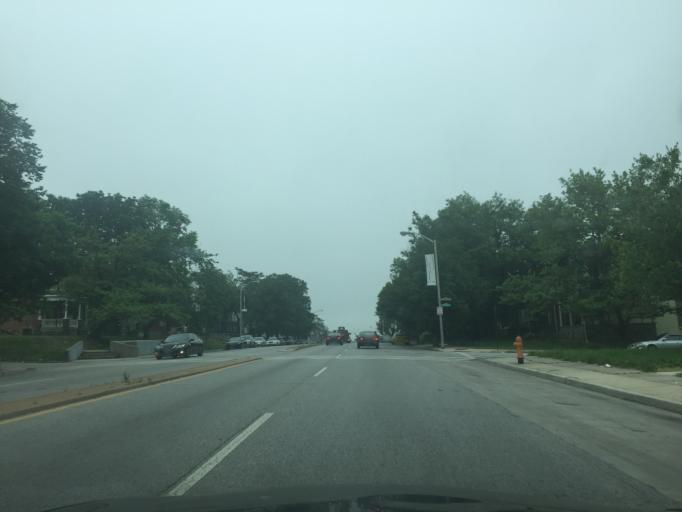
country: US
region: Maryland
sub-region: Baltimore County
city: Lochearn
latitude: 39.3324
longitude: -76.6611
